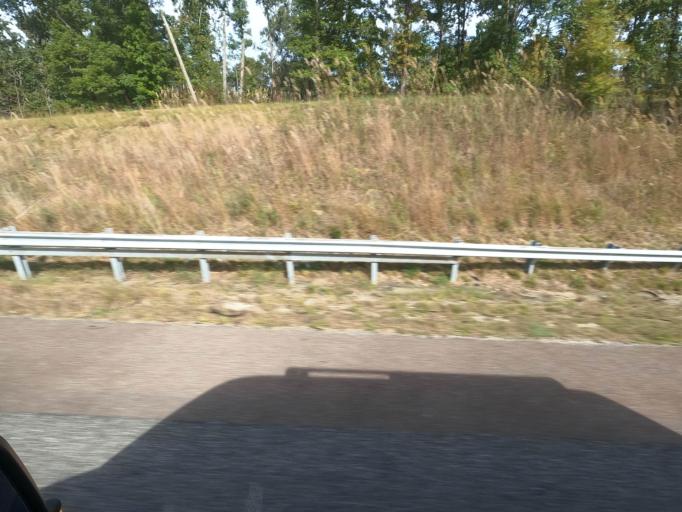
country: US
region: Tennessee
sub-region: Humphreys County
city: New Johnsonville
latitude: 35.8696
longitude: -87.9981
